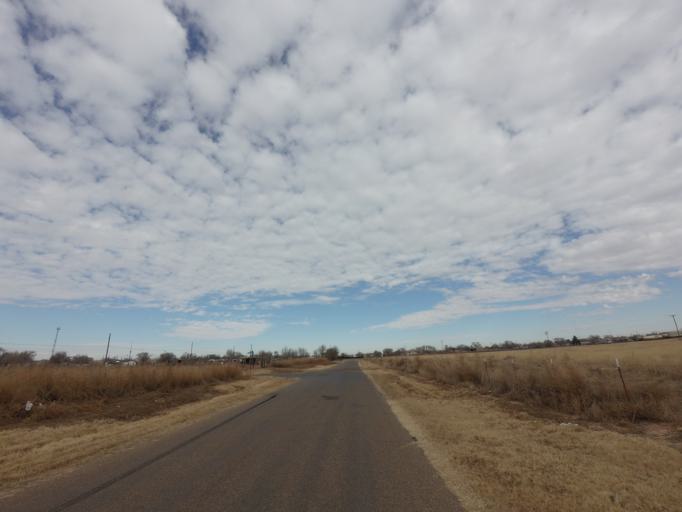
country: US
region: New Mexico
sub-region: Curry County
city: Clovis
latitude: 34.3962
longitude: -103.2267
